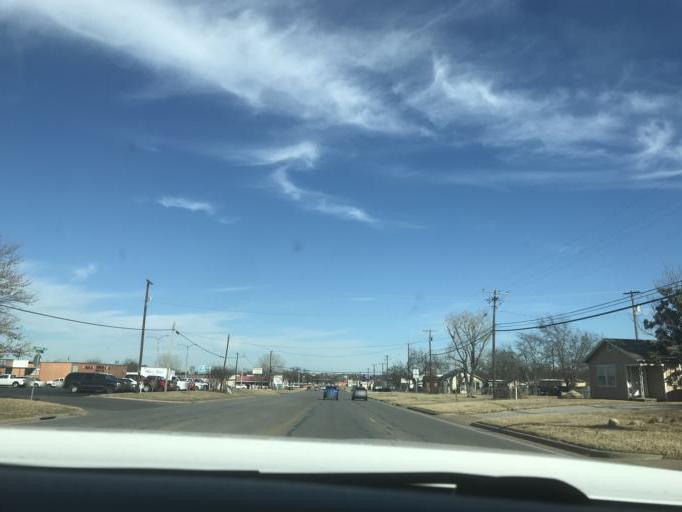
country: US
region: Texas
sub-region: Erath County
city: Stephenville
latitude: 32.2293
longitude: -98.2156
